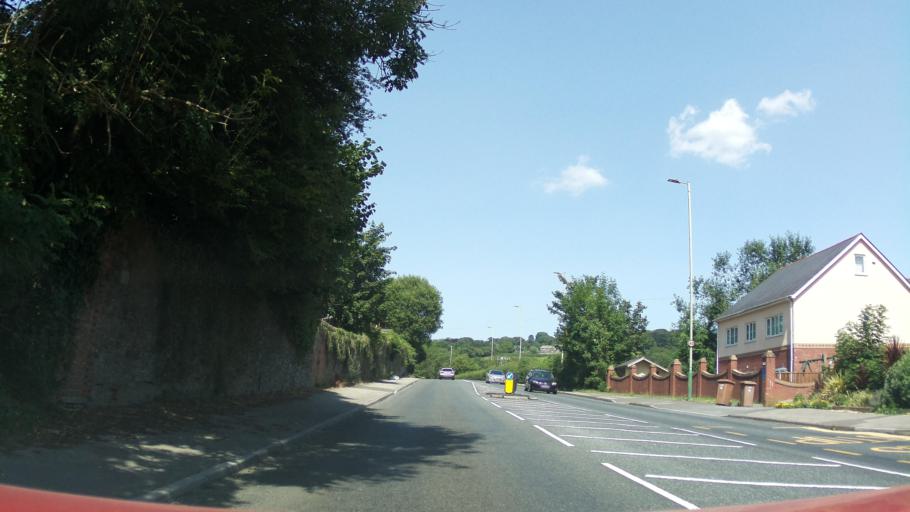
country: GB
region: Wales
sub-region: Caerphilly County Borough
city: Hengoed
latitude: 51.6475
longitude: -3.2235
